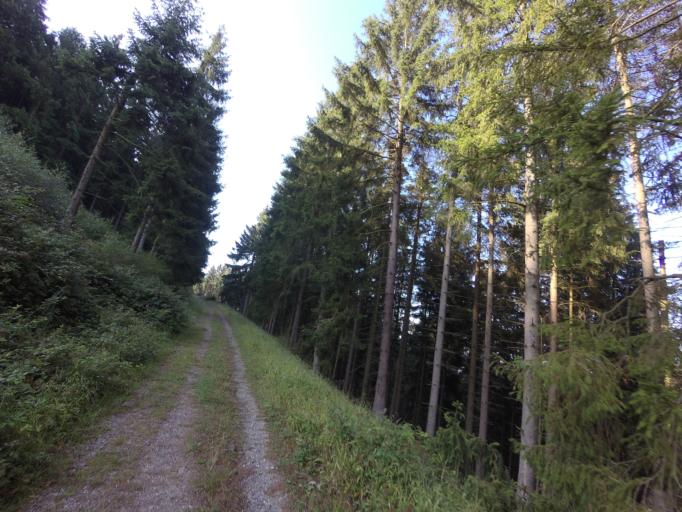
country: DE
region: North Rhine-Westphalia
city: Heimbach
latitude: 50.6122
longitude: 6.4090
